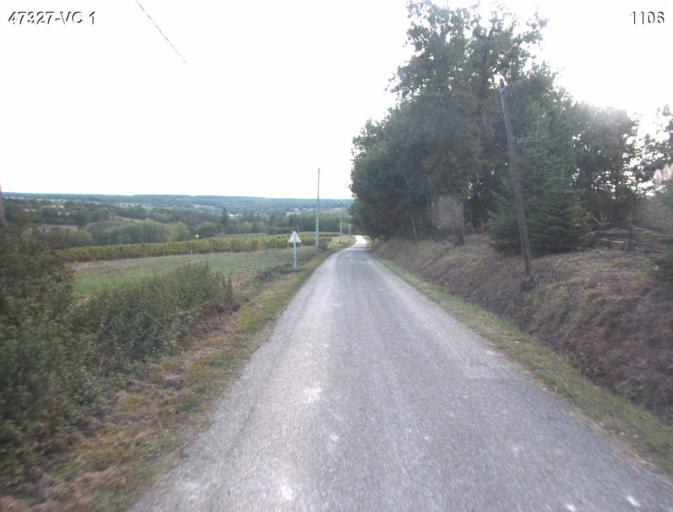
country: FR
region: Aquitaine
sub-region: Departement du Lot-et-Garonne
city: Barbaste
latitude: 44.1945
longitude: 0.2570
